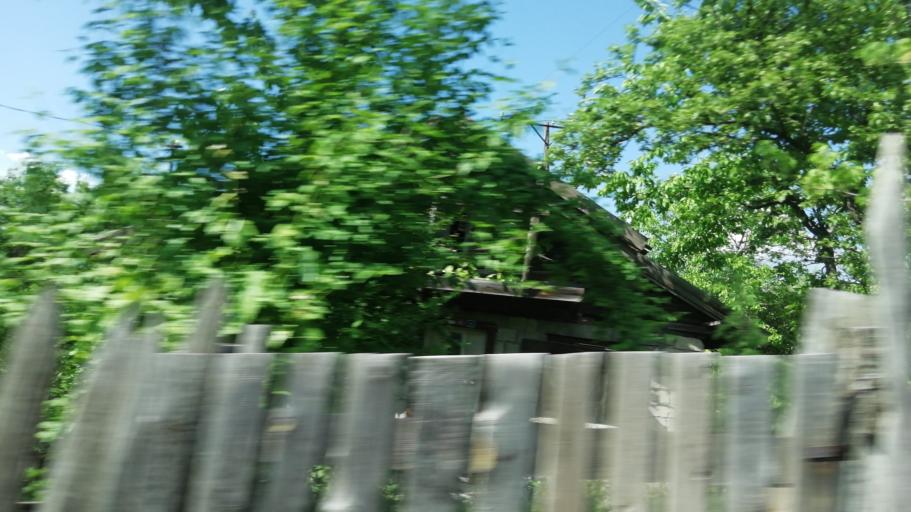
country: TR
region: Karabuk
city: Karabuk
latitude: 41.1255
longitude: 32.5787
